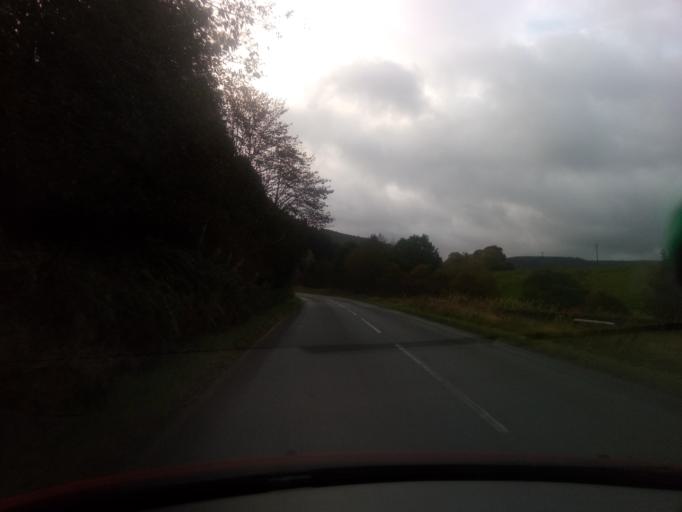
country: GB
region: Scotland
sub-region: The Scottish Borders
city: Hawick
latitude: 55.3533
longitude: -2.6477
